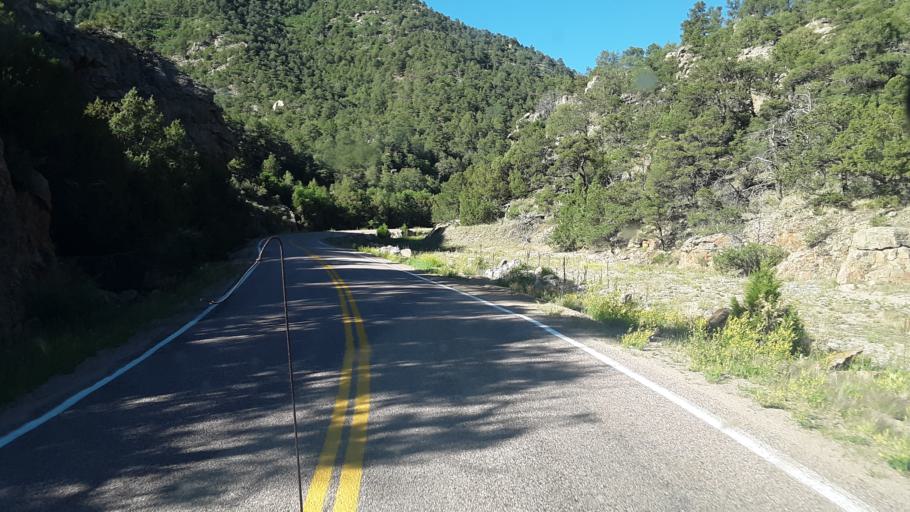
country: US
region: Colorado
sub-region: Fremont County
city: Canon City
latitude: 38.4230
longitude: -105.4063
